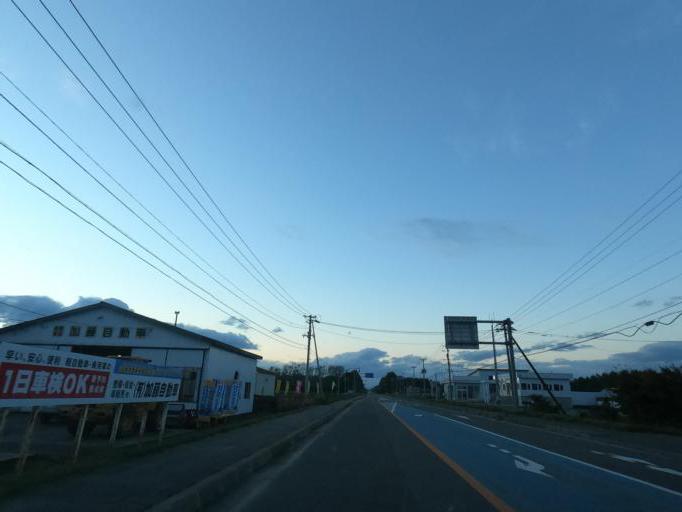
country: JP
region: Hokkaido
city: Obihiro
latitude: 42.6538
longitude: 143.1893
